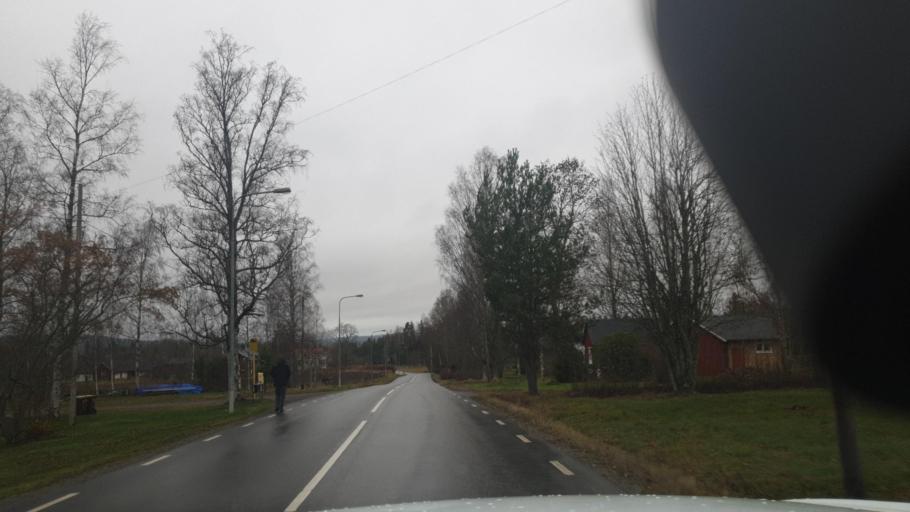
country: SE
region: Vaermland
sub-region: Arvika Kommun
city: Arvika
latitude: 59.5403
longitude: 12.5840
